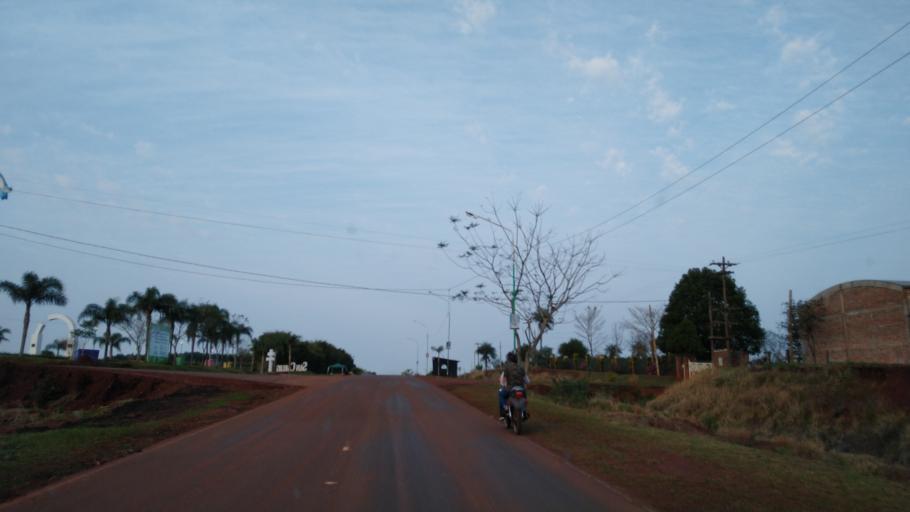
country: AR
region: Corrientes
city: San Carlos
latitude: -27.7517
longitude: -55.8882
